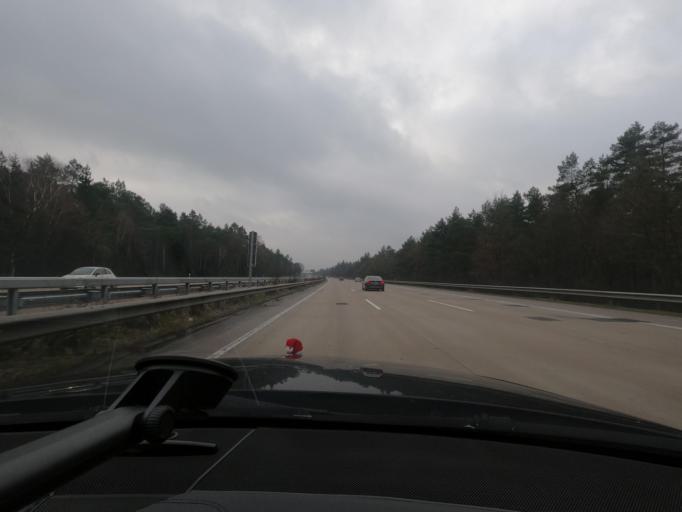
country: DE
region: Lower Saxony
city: Bispingen
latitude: 53.0722
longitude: 9.9581
